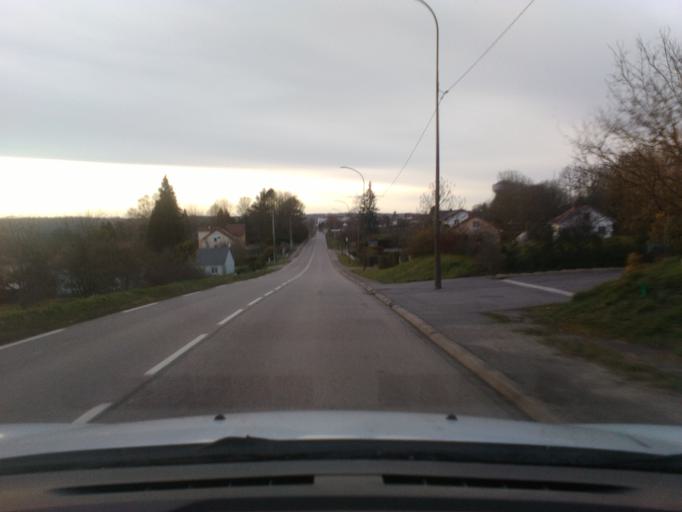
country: FR
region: Lorraine
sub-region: Departement des Vosges
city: Charmes
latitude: 48.3730
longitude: 6.3077
